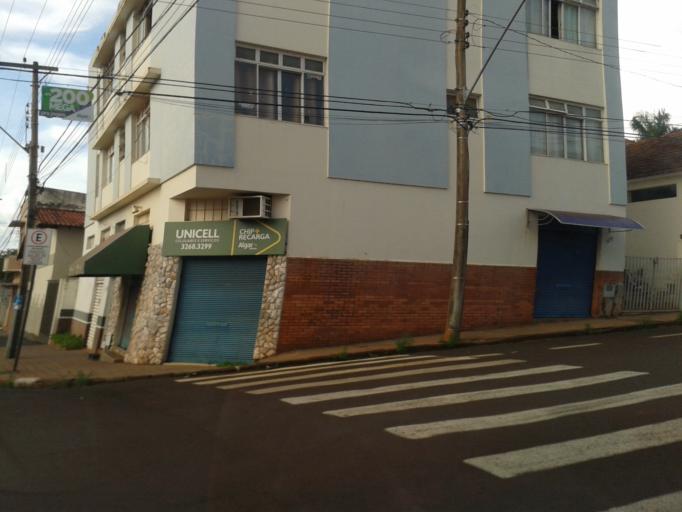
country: BR
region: Minas Gerais
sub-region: Ituiutaba
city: Ituiutaba
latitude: -18.9776
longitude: -49.4614
